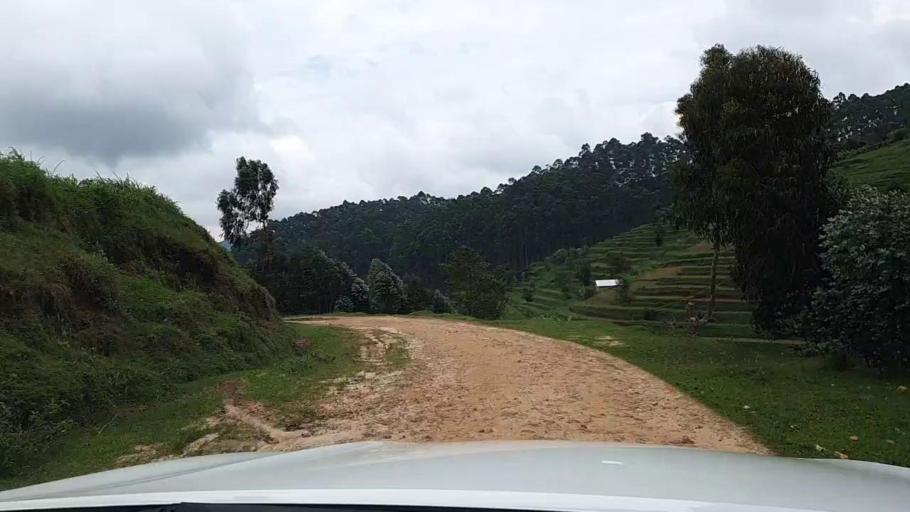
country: RW
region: Western Province
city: Kibuye
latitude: -2.2833
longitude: 29.3698
